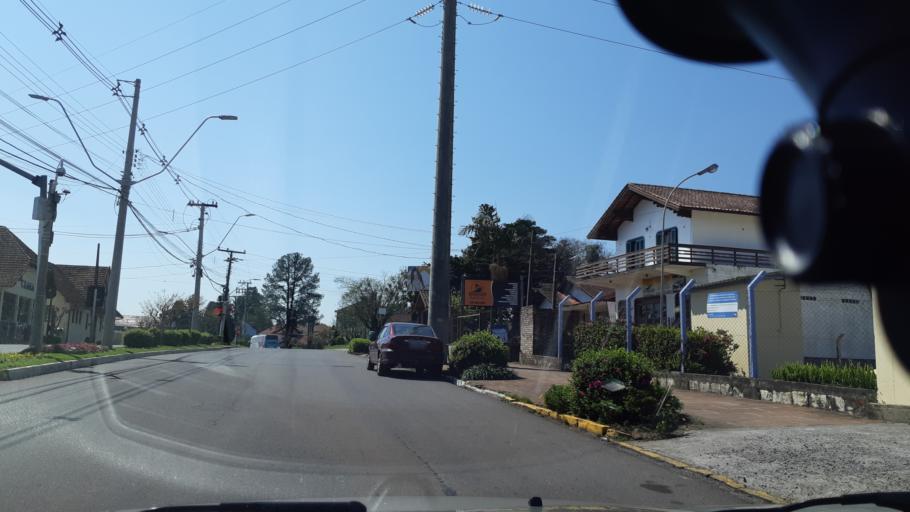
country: BR
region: Rio Grande do Sul
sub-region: Nova Petropolis
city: Nova Petropolis
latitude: -29.3829
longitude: -51.1173
